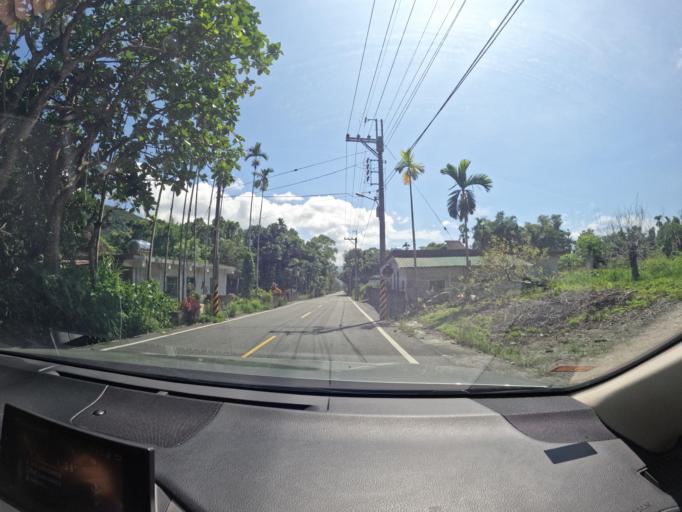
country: TW
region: Taiwan
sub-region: Hualien
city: Hualian
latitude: 23.5860
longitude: 121.3602
